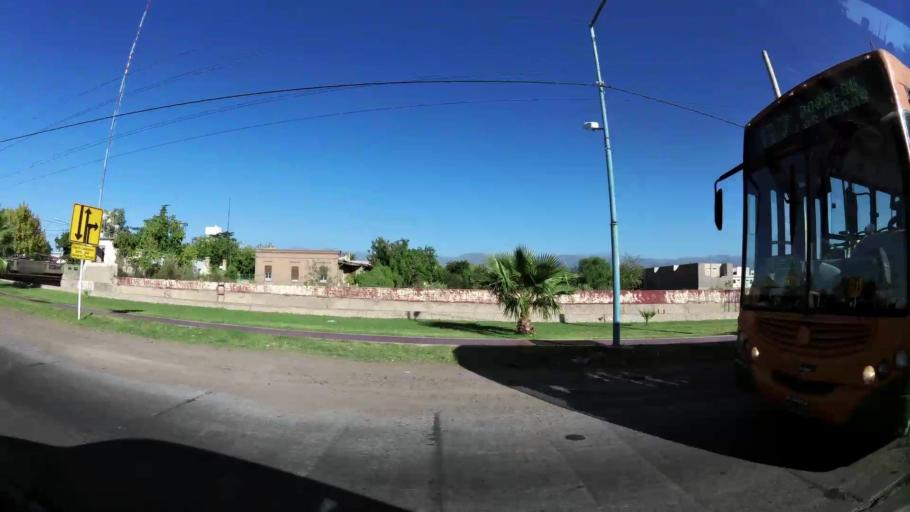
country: AR
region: Mendoza
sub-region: Departamento de Godoy Cruz
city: Godoy Cruz
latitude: -32.9302
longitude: -68.8390
